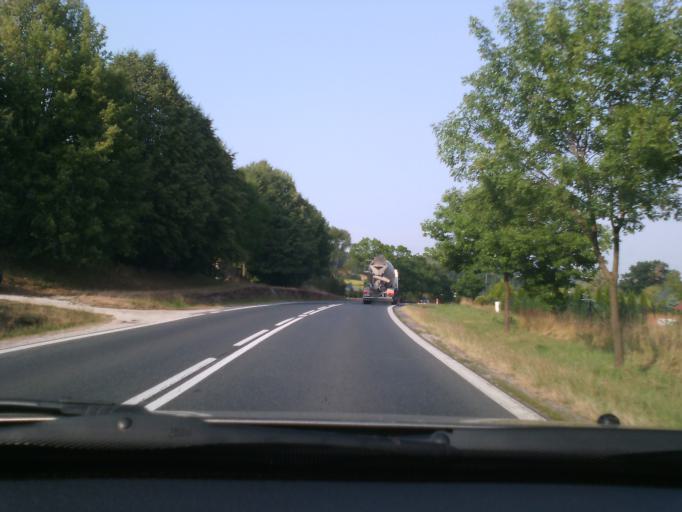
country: PL
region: Lower Silesian Voivodeship
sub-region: Powiat jeleniogorski
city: Piechowice
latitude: 50.8814
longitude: 15.6347
